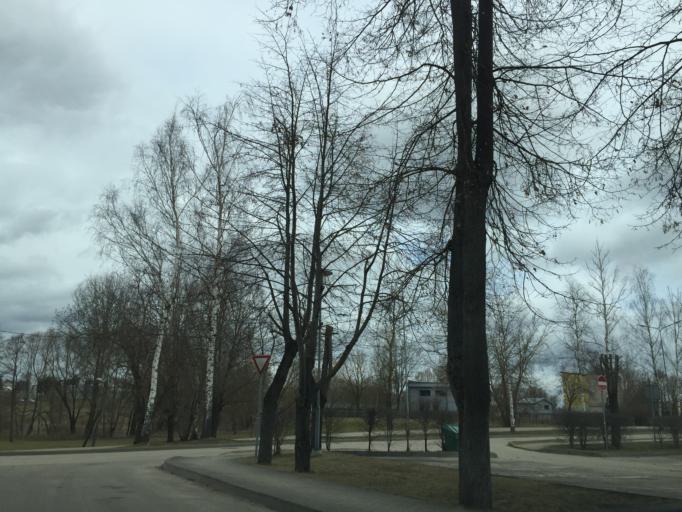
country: LV
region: Livani
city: Livani
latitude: 56.3544
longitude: 26.1705
